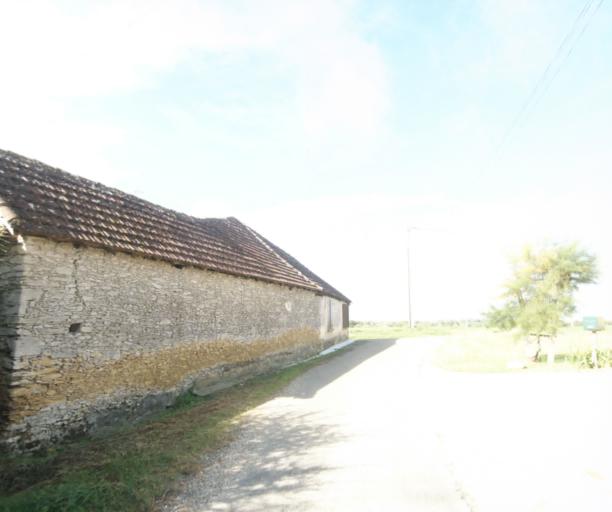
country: FR
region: Midi-Pyrenees
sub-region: Departement du Gers
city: Cazaubon
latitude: 43.8577
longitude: -0.0846
